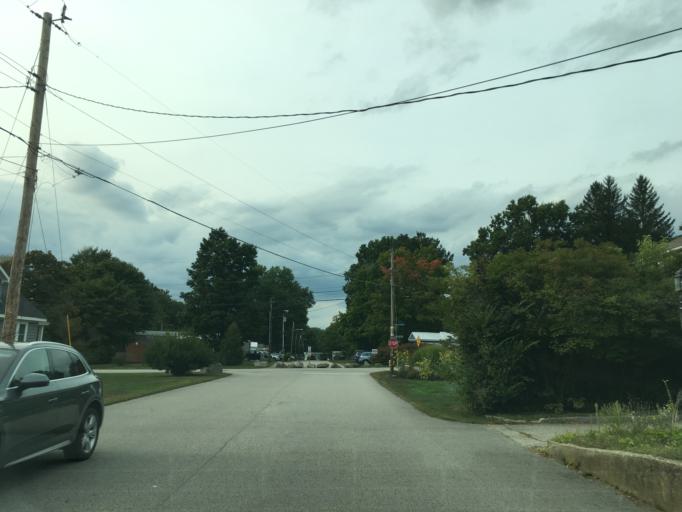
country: US
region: New Hampshire
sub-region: Rockingham County
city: Exeter
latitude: 42.9854
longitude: -70.9431
